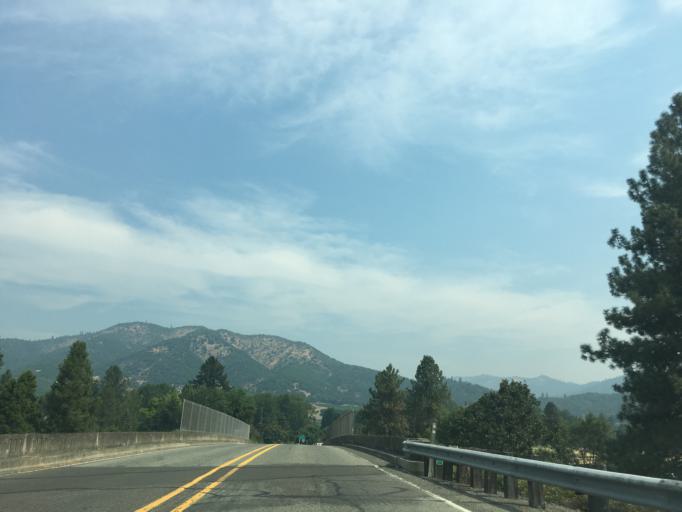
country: US
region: Oregon
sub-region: Jackson County
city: Gold Hill
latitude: 42.4277
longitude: -123.0975
